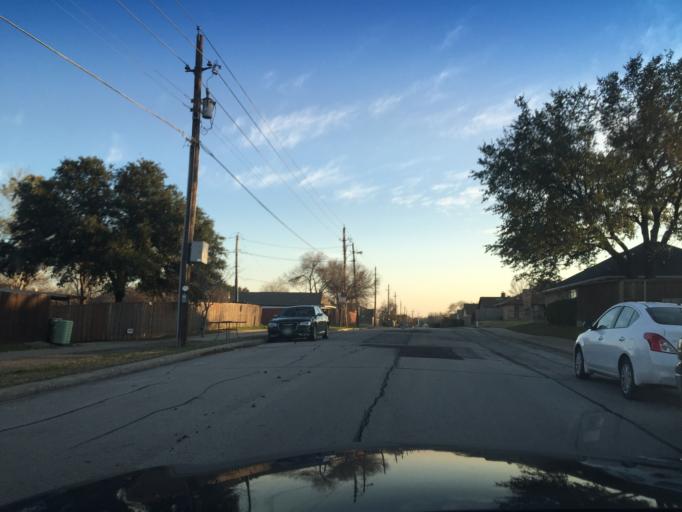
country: US
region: Texas
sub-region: Dallas County
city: Carrollton
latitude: 32.9903
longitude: -96.8777
